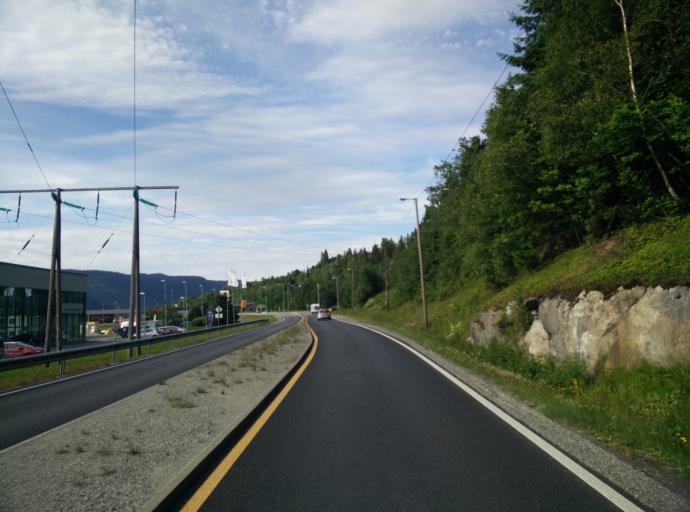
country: NO
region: Sor-Trondelag
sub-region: Orkdal
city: Orkanger
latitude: 63.2947
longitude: 9.8532
